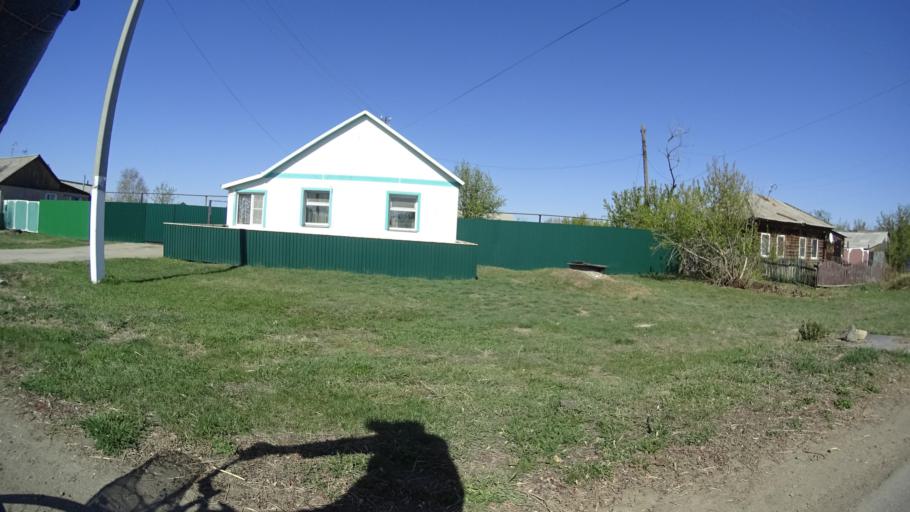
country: RU
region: Chelyabinsk
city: Chesma
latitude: 53.7995
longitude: 61.0242
